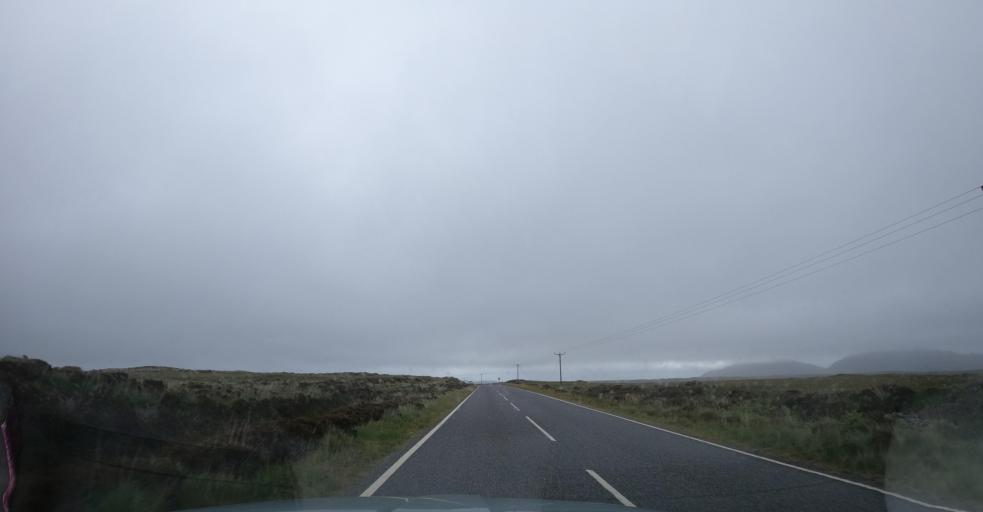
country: GB
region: Scotland
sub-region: Eilean Siar
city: Isle of North Uist
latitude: 57.5873
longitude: -7.2316
